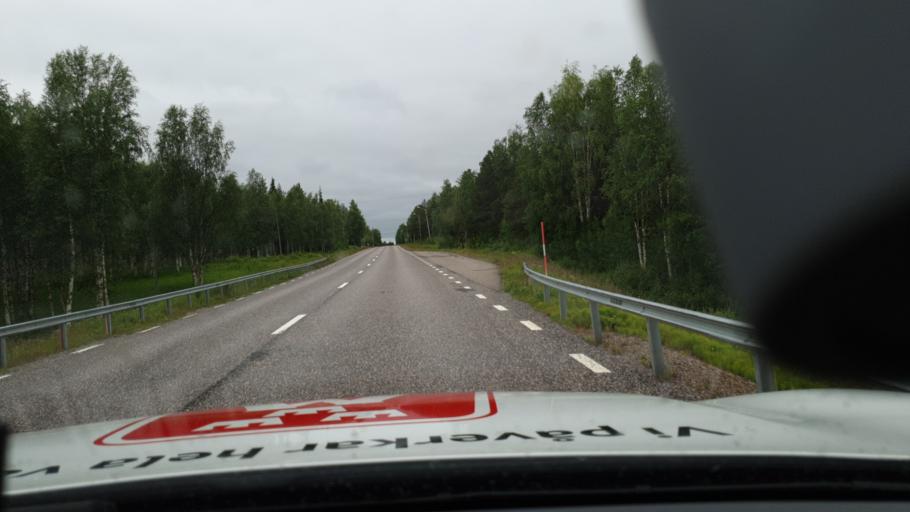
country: SE
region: Norrbotten
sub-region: Pajala Kommun
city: Pajala
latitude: 67.1889
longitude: 23.4774
